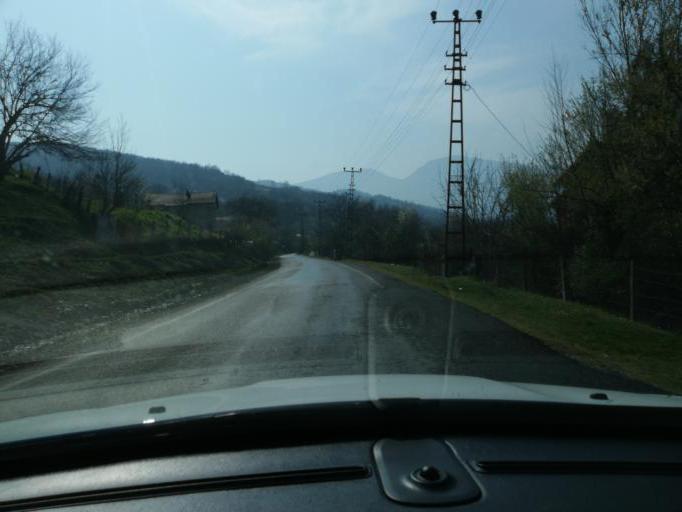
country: TR
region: Karabuk
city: Yenice
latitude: 41.2413
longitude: 32.3576
